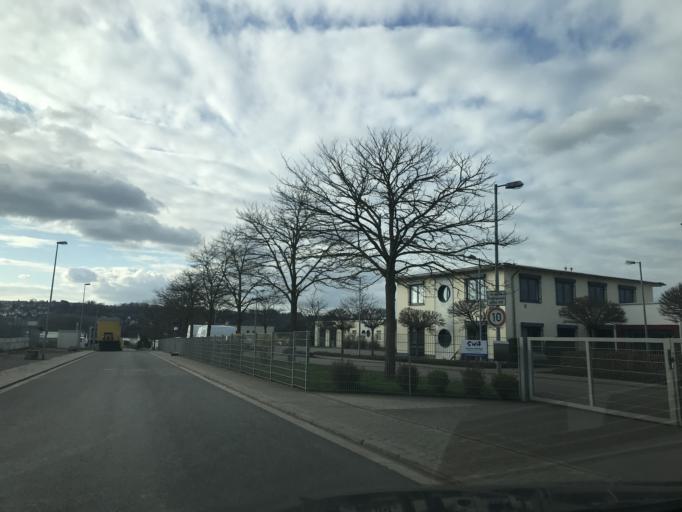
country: DE
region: Saarland
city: Blieskastel
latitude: 49.2350
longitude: 7.2773
